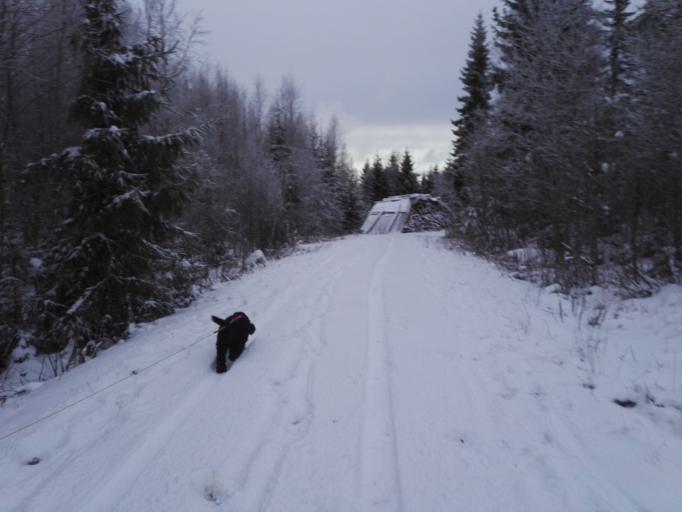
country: FI
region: Satakunta
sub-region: Pohjois-Satakunta
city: Jaemijaervi
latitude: 61.7819
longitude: 22.8707
